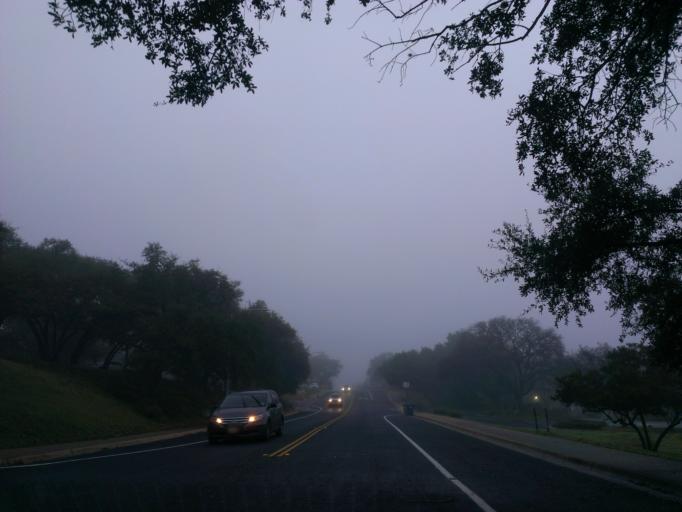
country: US
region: Texas
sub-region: Williamson County
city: Jollyville
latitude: 30.3746
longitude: -97.7893
